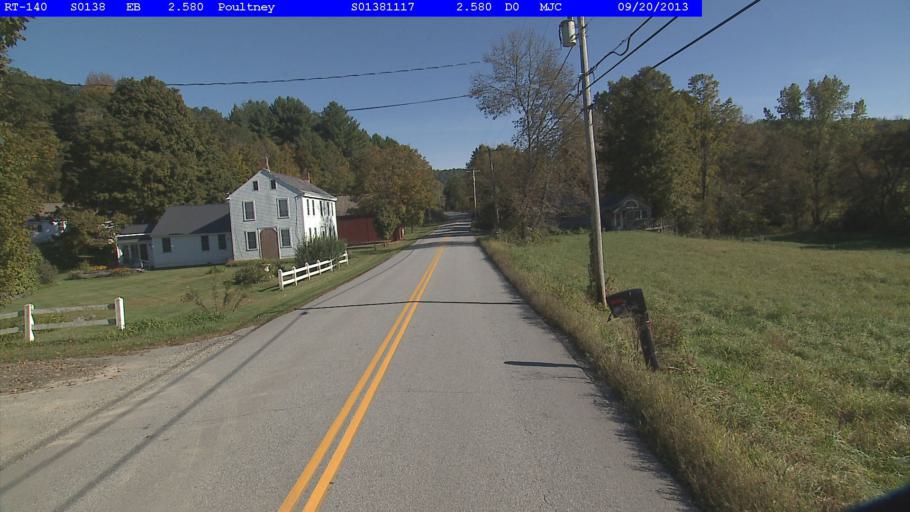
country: US
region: Vermont
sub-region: Rutland County
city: Poultney
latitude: 43.5251
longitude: -73.1873
